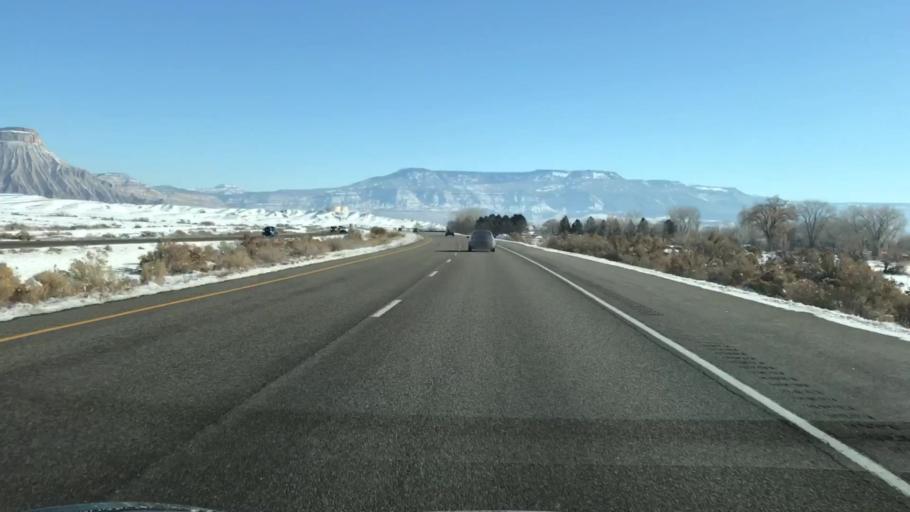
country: US
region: Colorado
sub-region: Mesa County
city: Fruitvale
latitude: 39.1052
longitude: -108.4858
